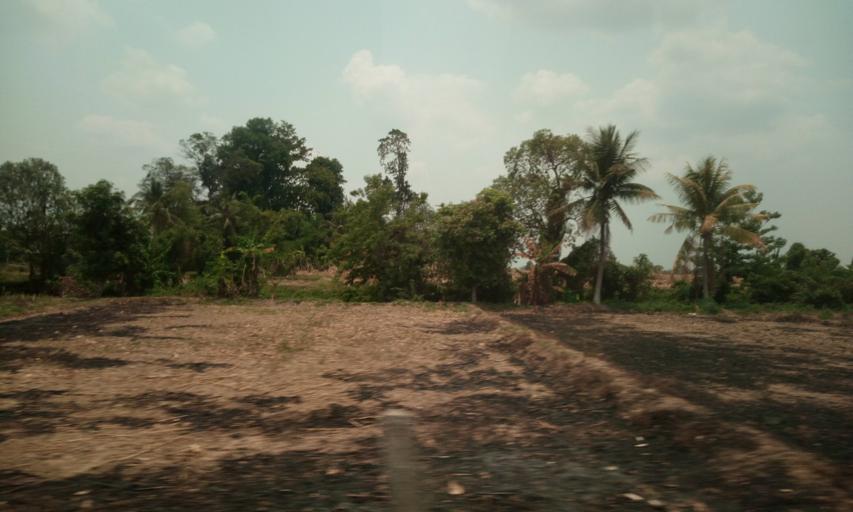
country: TH
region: Phayao
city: Phu Sang
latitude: 19.6140
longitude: 100.3229
